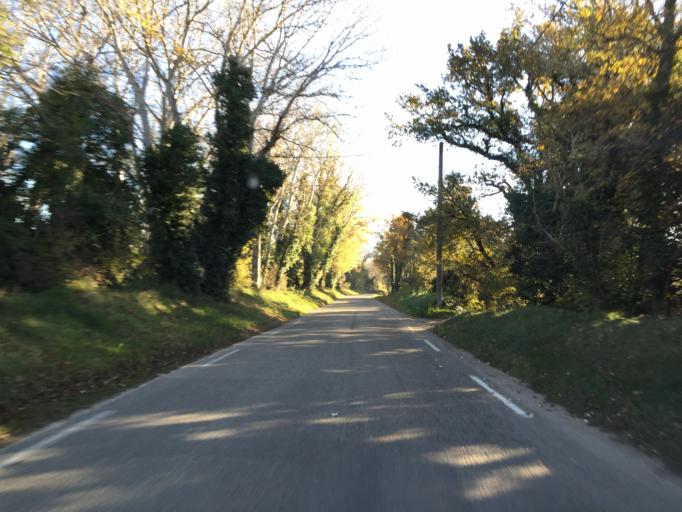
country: FR
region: Provence-Alpes-Cote d'Azur
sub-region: Departement du Vaucluse
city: Bedarrides
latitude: 44.0390
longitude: 4.9117
